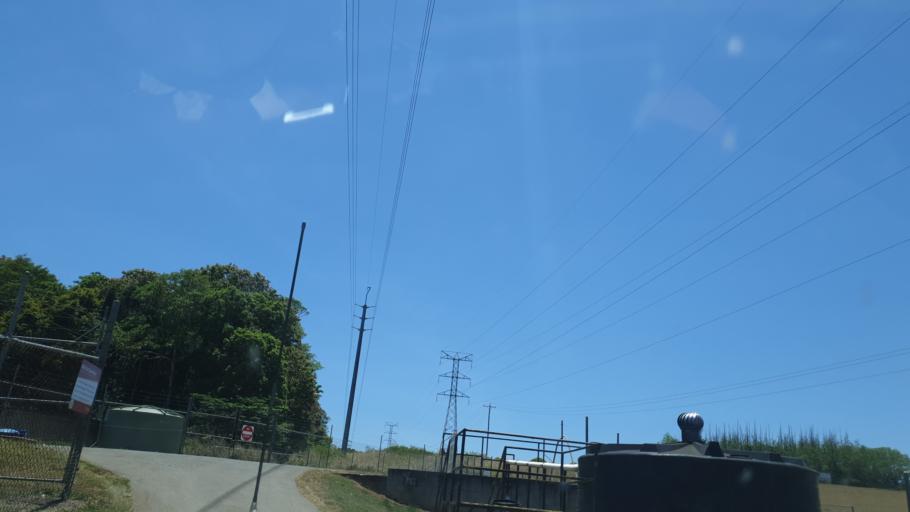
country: AU
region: Queensland
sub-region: Tablelands
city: Atherton
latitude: -17.2547
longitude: 145.4801
